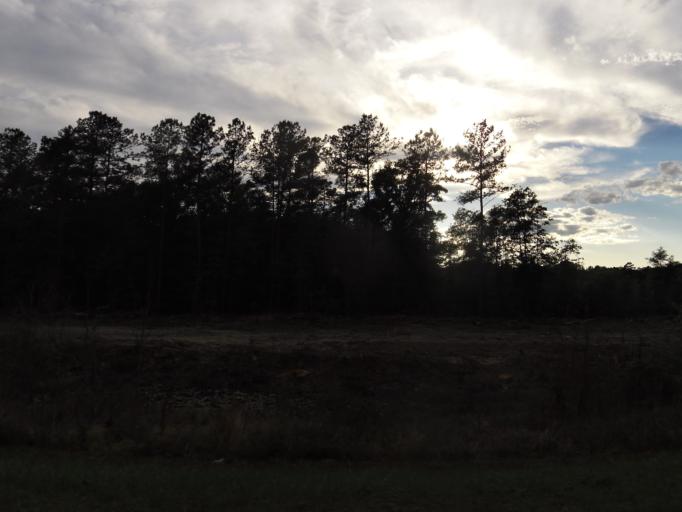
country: US
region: South Carolina
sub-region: Jasper County
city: Hardeeville
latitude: 32.4017
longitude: -81.0996
